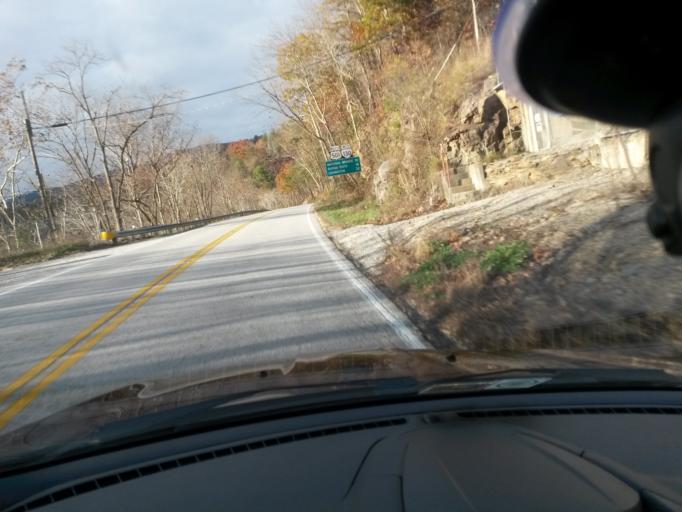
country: US
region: Virginia
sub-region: Rockbridge County
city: Glasgow
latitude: 37.5929
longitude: -79.3805
